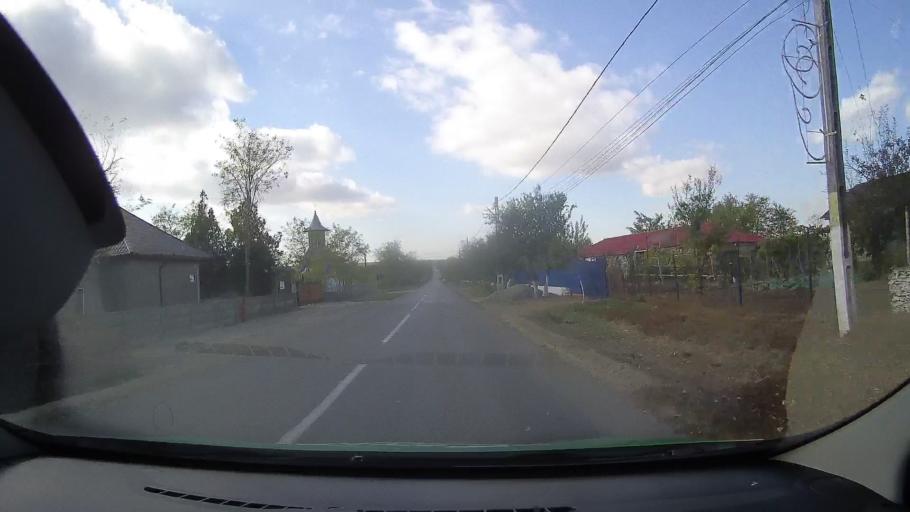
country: RO
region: Constanta
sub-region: Comuna Sacele
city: Sacele
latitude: 44.4898
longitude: 28.6515
